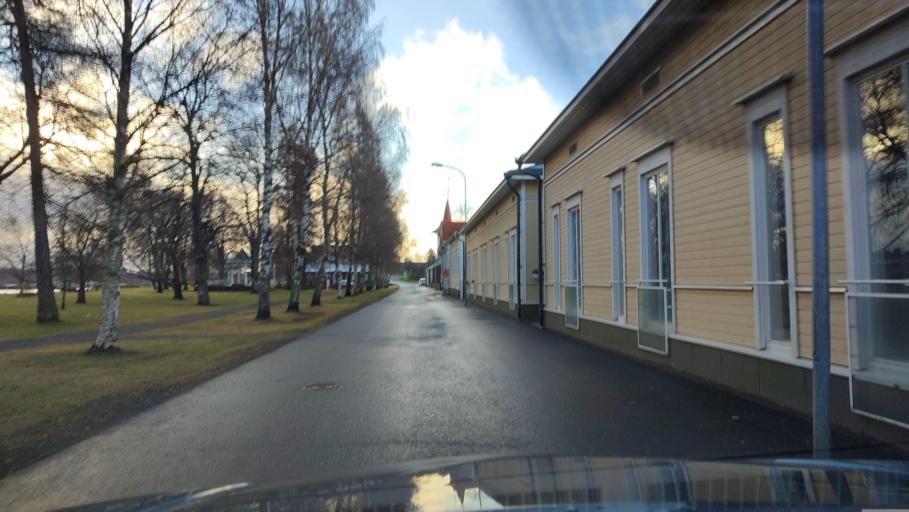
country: FI
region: Ostrobothnia
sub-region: Sydosterbotten
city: Kristinestad
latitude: 62.2699
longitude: 21.3775
